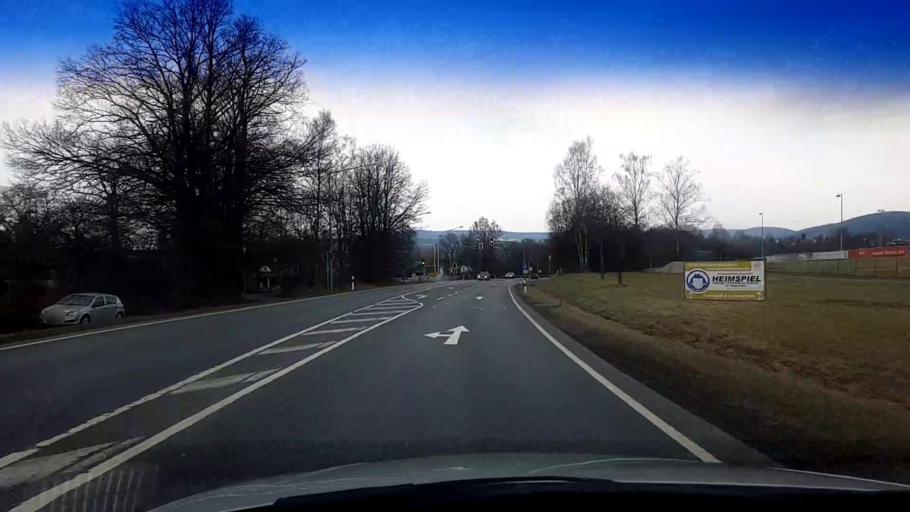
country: DE
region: Bavaria
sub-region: Upper Franconia
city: Kulmbach
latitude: 50.0880
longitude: 11.4556
